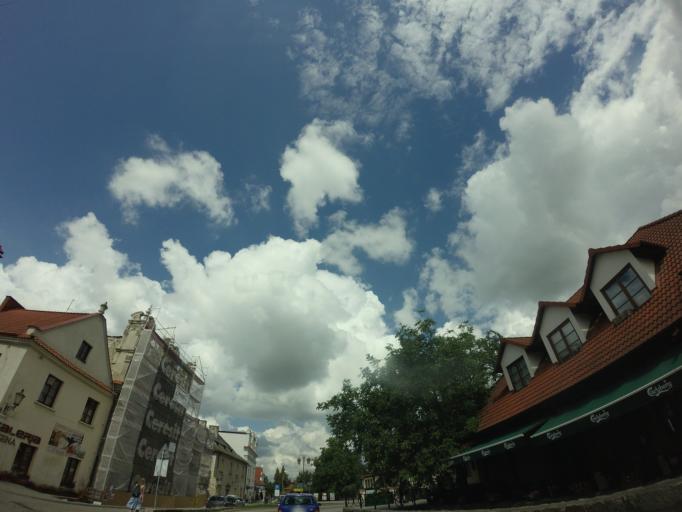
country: PL
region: Lublin Voivodeship
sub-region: Powiat pulawski
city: Kazimierz Dolny
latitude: 51.3220
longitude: 21.9460
